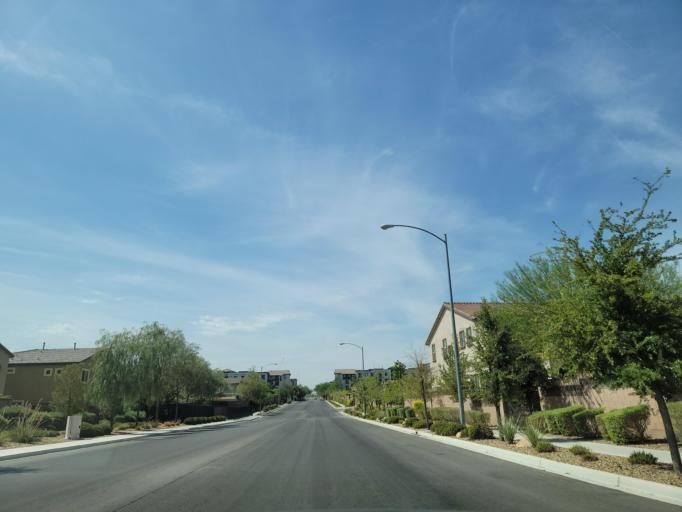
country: US
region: Nevada
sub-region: Clark County
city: Spring Valley
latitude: 36.0766
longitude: -115.2840
